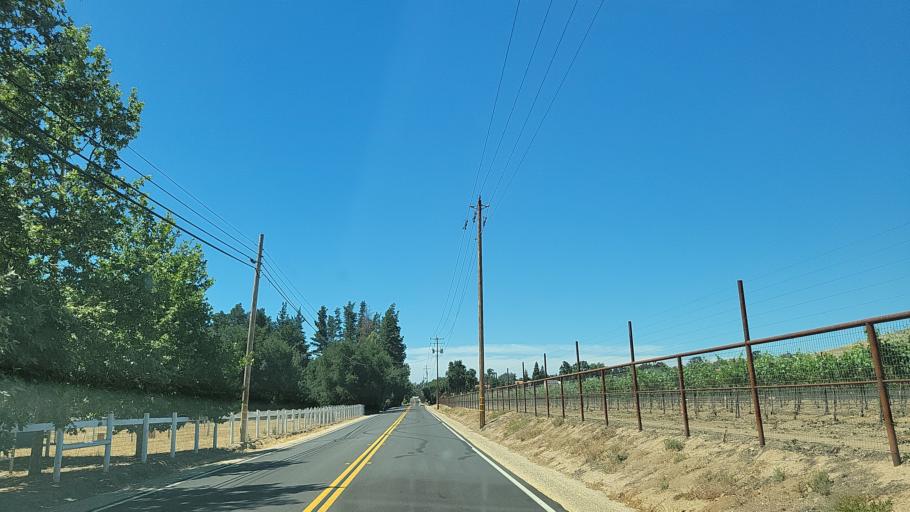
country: US
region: California
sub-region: San Luis Obispo County
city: Atascadero
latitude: 35.4954
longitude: -120.6456
